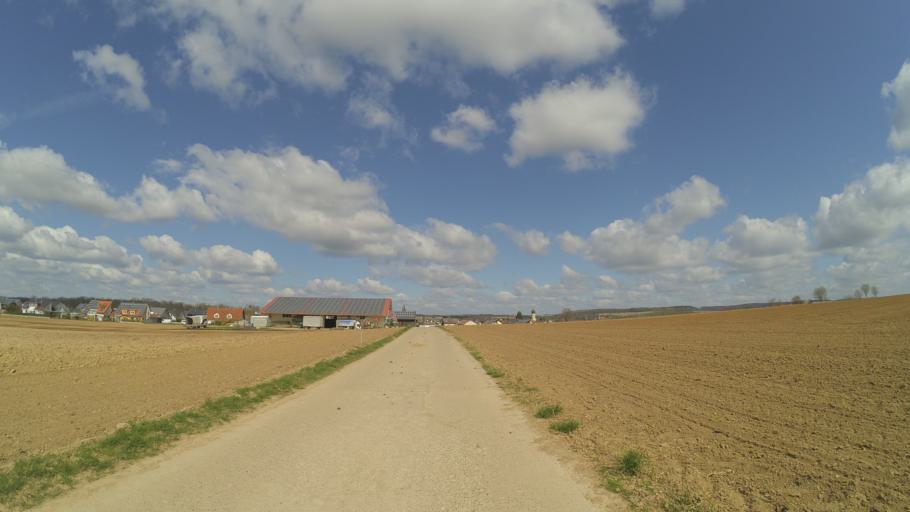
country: DE
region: Baden-Wuerttemberg
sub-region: Regierungsbezirk Stuttgart
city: Oedheim
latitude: 49.2447
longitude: 9.2870
